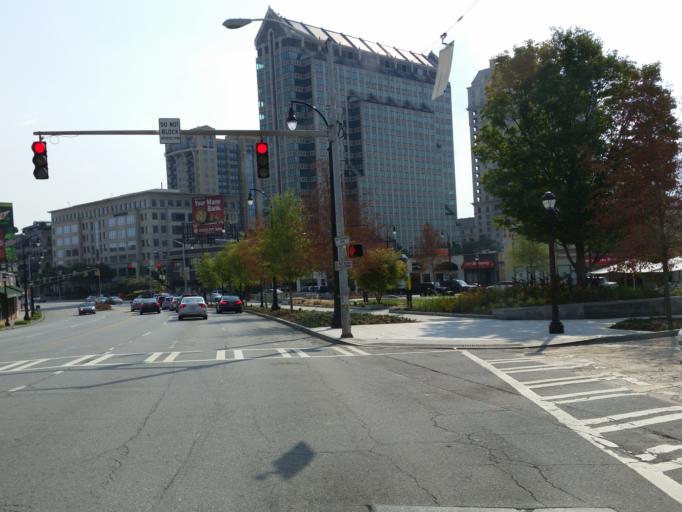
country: US
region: Georgia
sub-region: DeKalb County
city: North Atlanta
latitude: 33.8403
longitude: -84.3786
